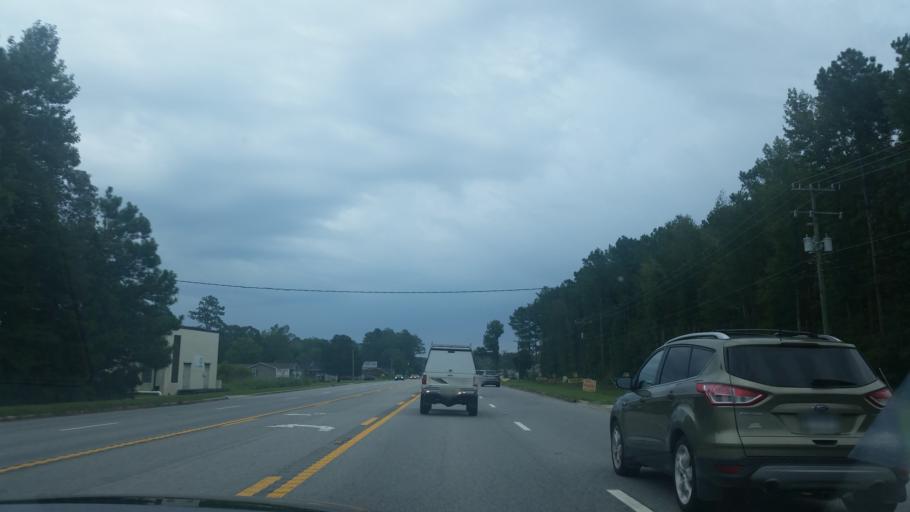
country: US
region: North Carolina
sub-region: Currituck County
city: Currituck
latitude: 36.4545
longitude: -76.0823
